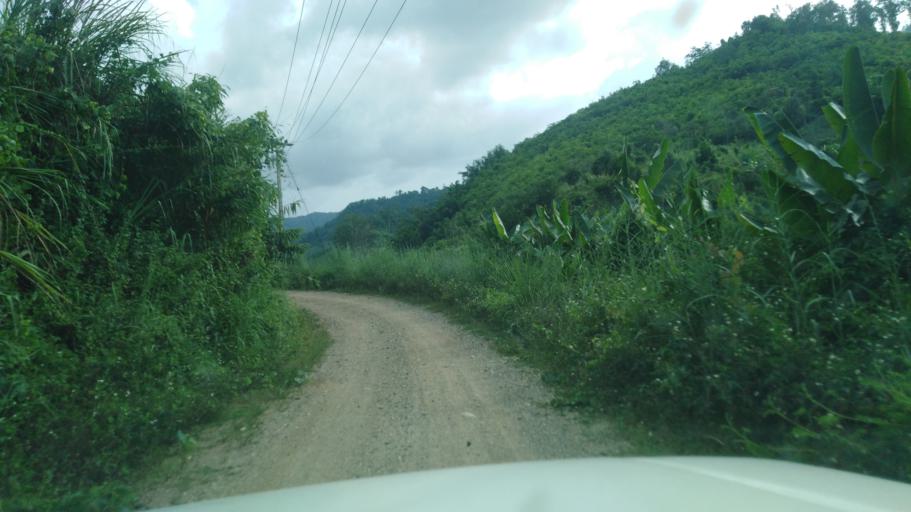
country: TH
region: Chiang Rai
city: Wiang Kaen
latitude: 19.7746
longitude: 100.6549
